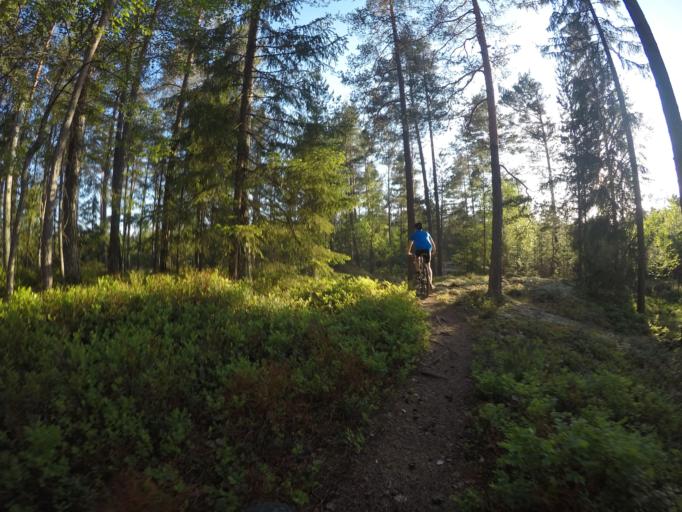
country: SE
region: Soedermanland
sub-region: Eskilstuna Kommun
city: Eskilstuna
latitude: 59.3345
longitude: 16.5236
